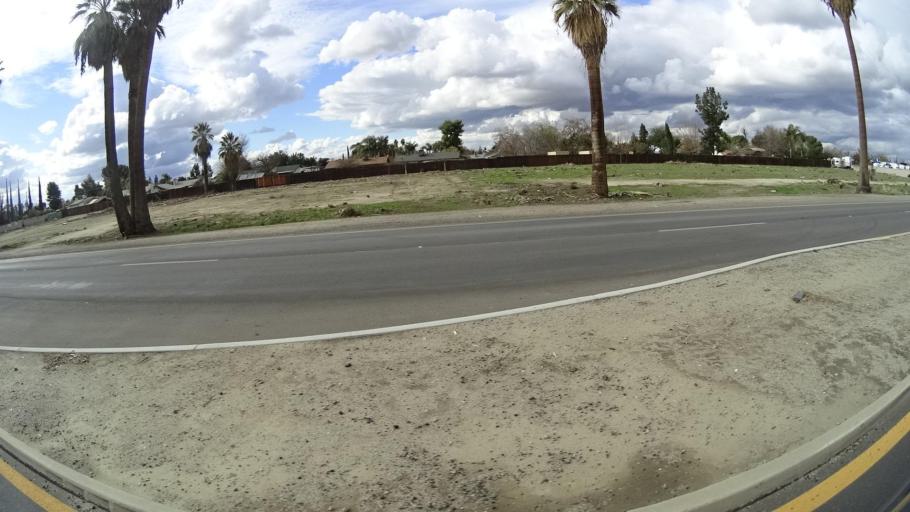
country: US
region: California
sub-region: Kern County
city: Greenfield
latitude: 35.2695
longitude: -119.0030
